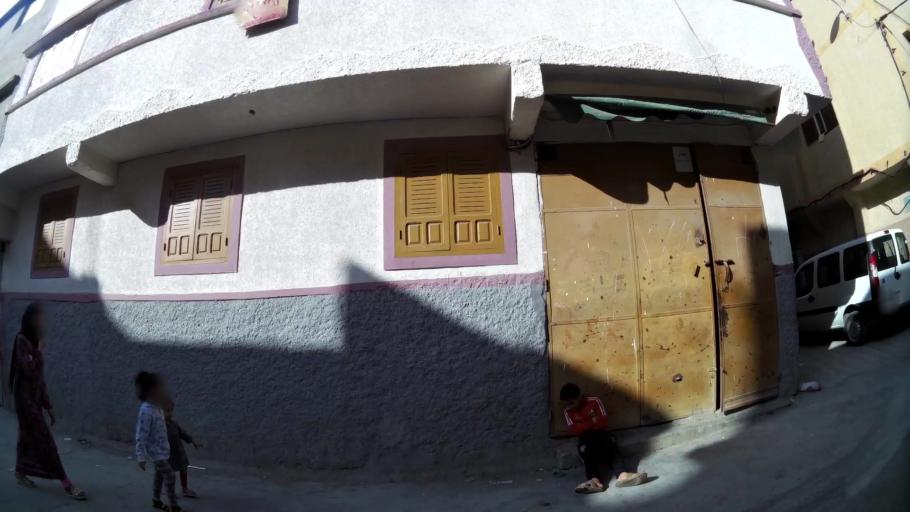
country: MA
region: Rabat-Sale-Zemmour-Zaer
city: Sale
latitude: 34.0542
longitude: -6.7745
